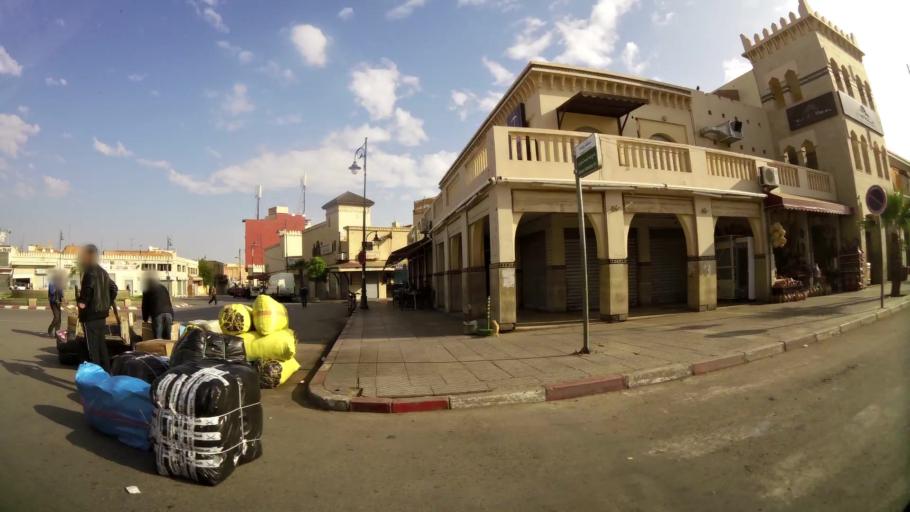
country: MA
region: Oriental
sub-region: Oujda-Angad
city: Oujda
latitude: 34.6815
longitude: -1.9104
